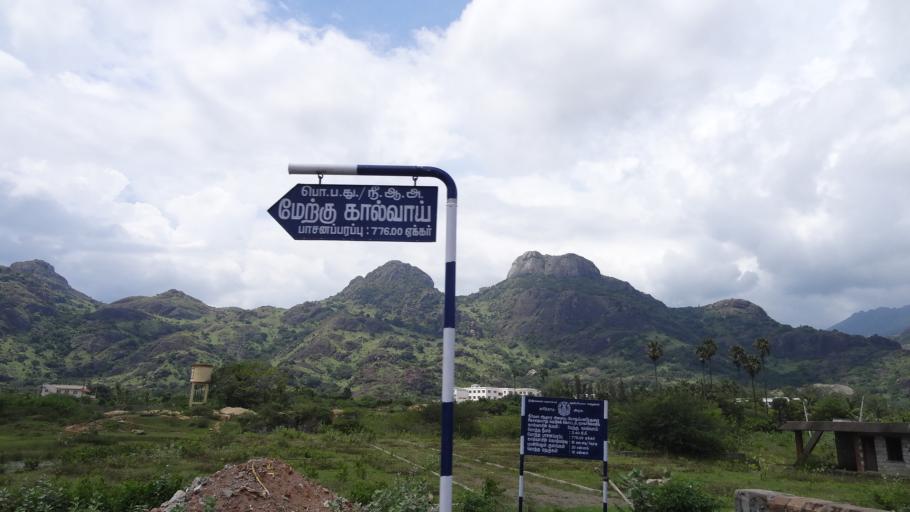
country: IN
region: Tamil Nadu
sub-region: Kanniyakumari
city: Nagercoil
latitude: 8.2050
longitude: 77.4021
